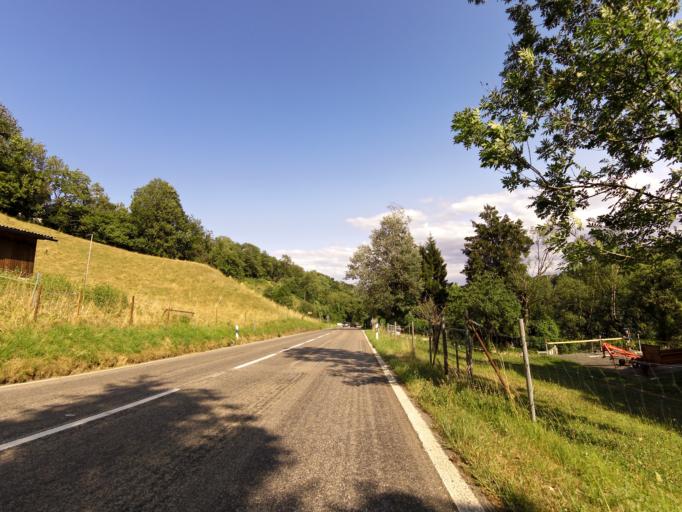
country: CH
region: Solothurn
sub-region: Bezirk Goesgen
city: Trimbach
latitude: 47.3704
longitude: 7.8755
